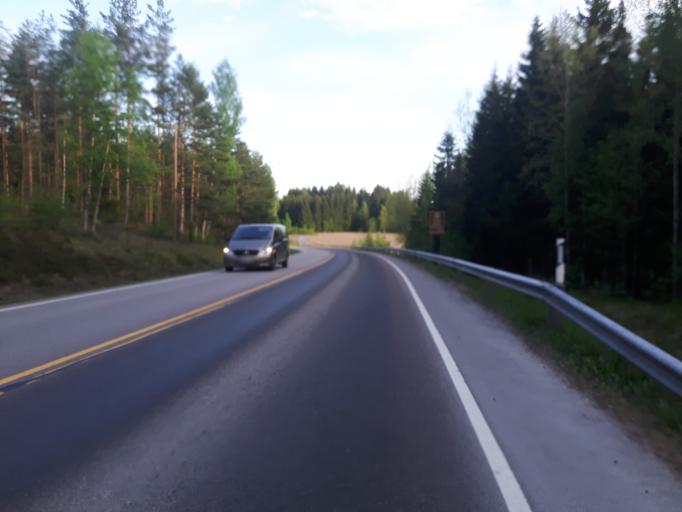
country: FI
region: Uusimaa
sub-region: Loviisa
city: Perna
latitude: 60.4669
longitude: 26.0310
